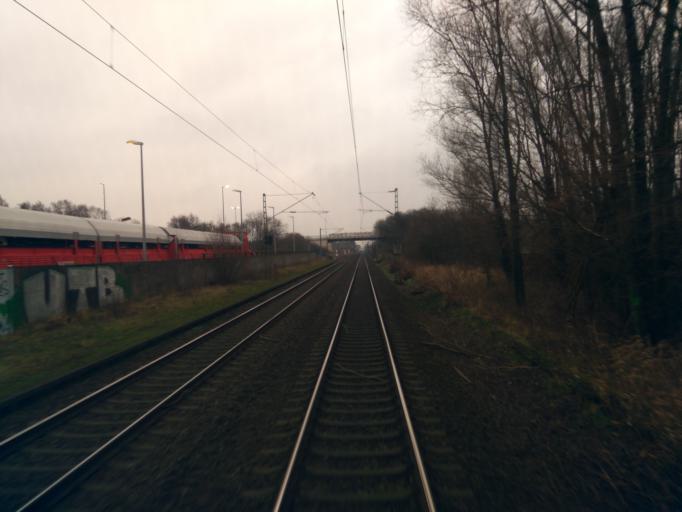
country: DE
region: Lower Saxony
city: Lilienthal
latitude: 53.0485
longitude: 8.9158
